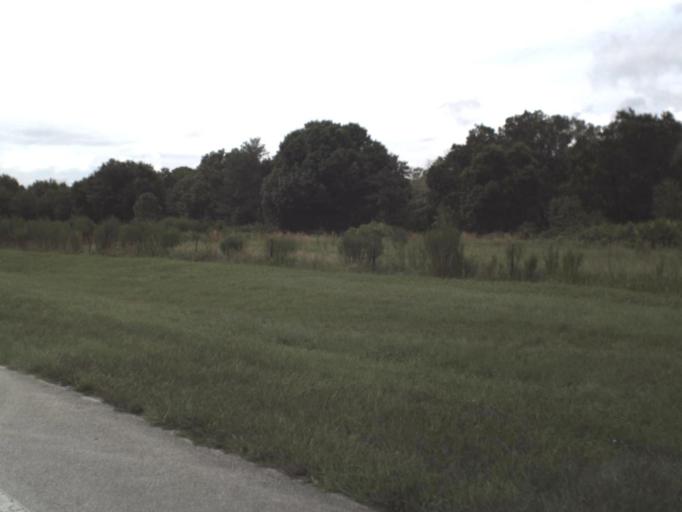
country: US
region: Florida
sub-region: Hillsborough County
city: Balm
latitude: 27.5890
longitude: -82.0933
